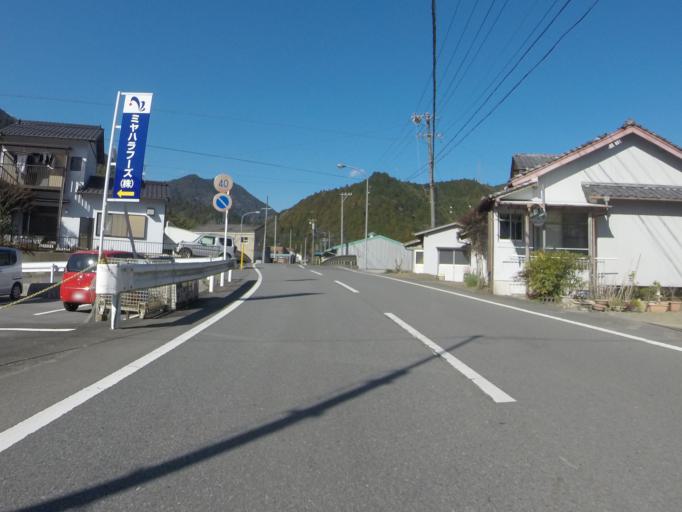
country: JP
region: Shizuoka
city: Fujinomiya
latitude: 35.1226
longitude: 138.4800
